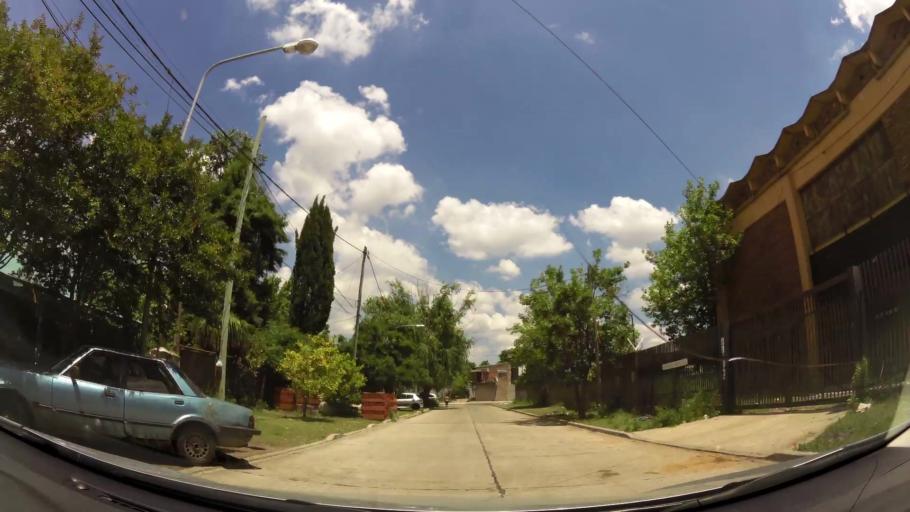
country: AR
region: Buenos Aires
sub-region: Partido de Tigre
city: Tigre
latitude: -34.4063
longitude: -58.5952
